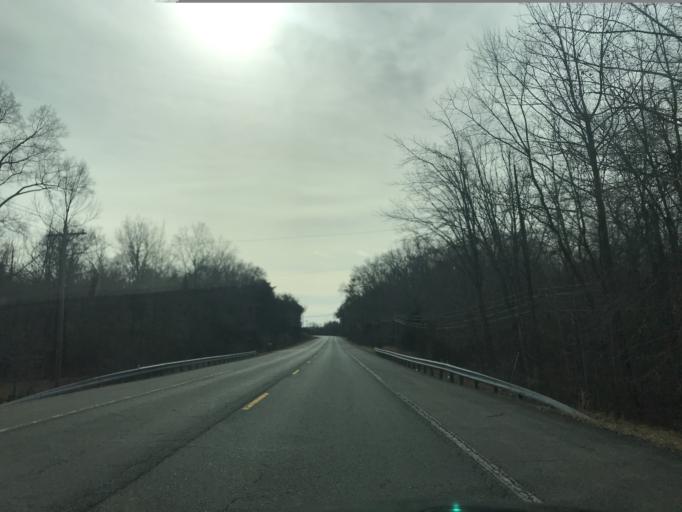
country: US
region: Virginia
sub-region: Prince William County
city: Cherry Hill
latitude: 38.4833
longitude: -77.2297
